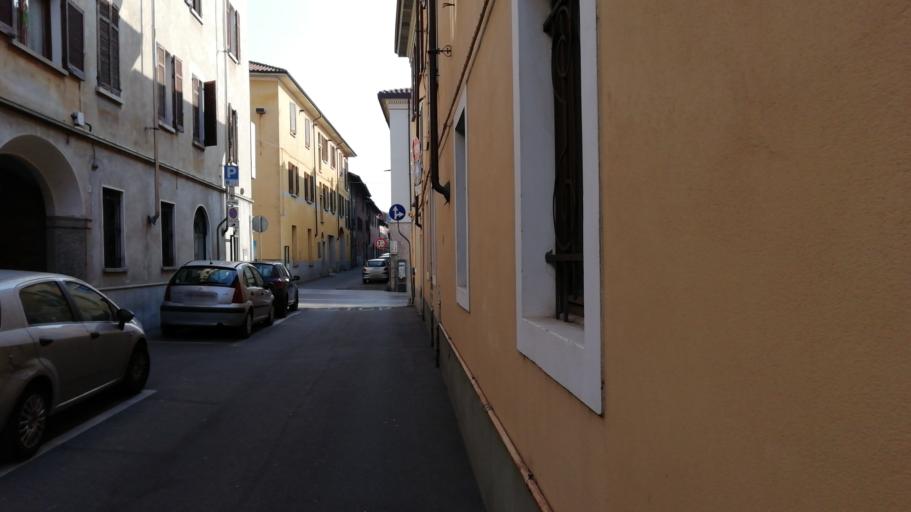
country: IT
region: Piedmont
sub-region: Provincia di Novara
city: Borgomanero
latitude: 45.6985
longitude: 8.4611
